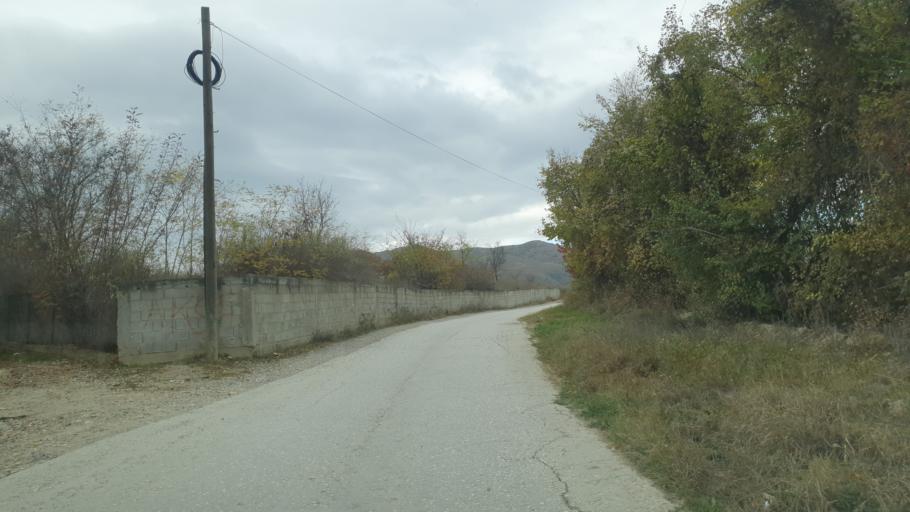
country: MK
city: Kondovo
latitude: 42.0383
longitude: 21.2804
